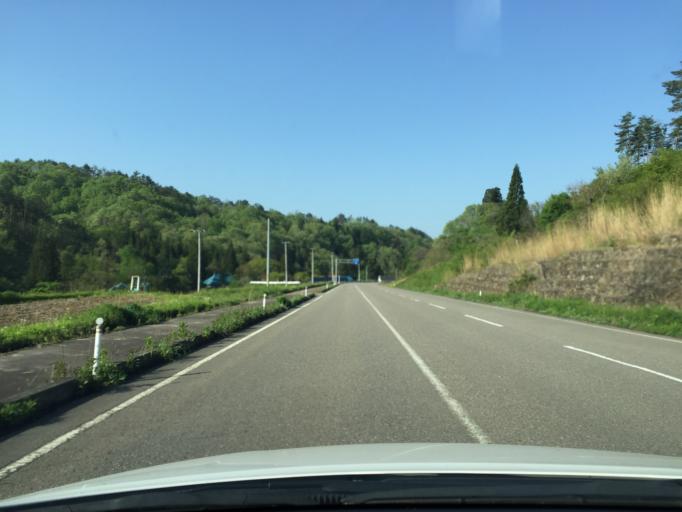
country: JP
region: Fukushima
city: Kitakata
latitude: 37.6699
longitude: 139.8137
